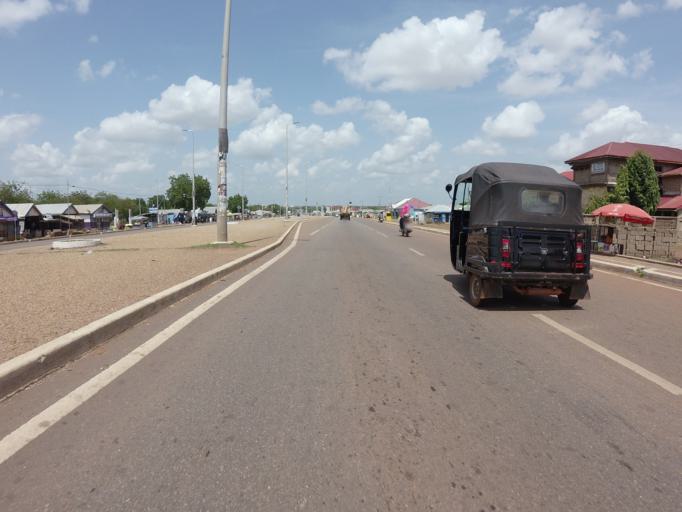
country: GH
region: Northern
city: Tamale
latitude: 9.3923
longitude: -0.8194
